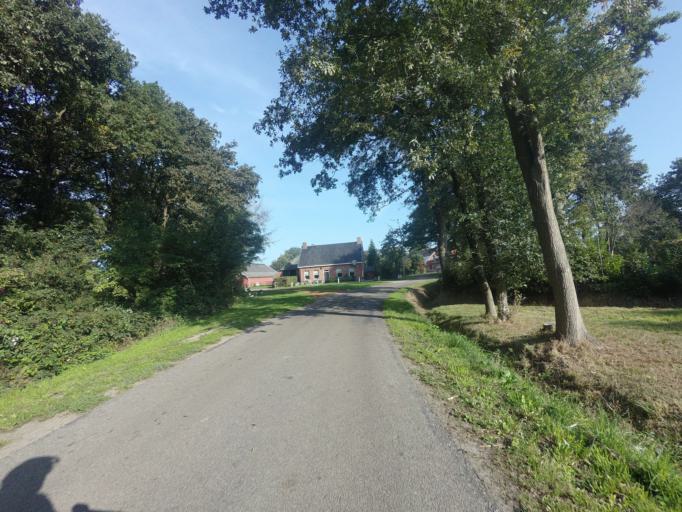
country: NL
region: Groningen
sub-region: Gemeente Leek
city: Leek
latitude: 53.1565
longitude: 6.4333
